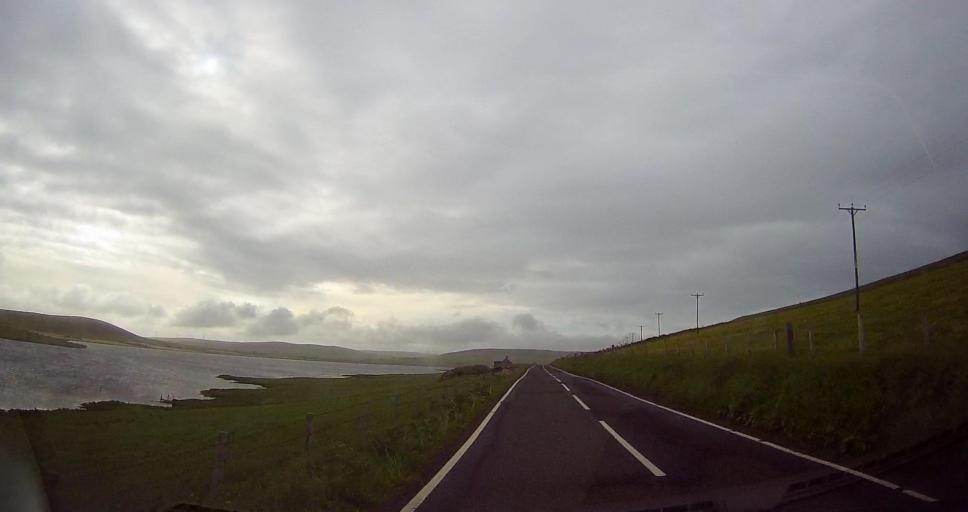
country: GB
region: Scotland
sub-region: Orkney Islands
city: Stromness
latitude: 59.1132
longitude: -3.2982
